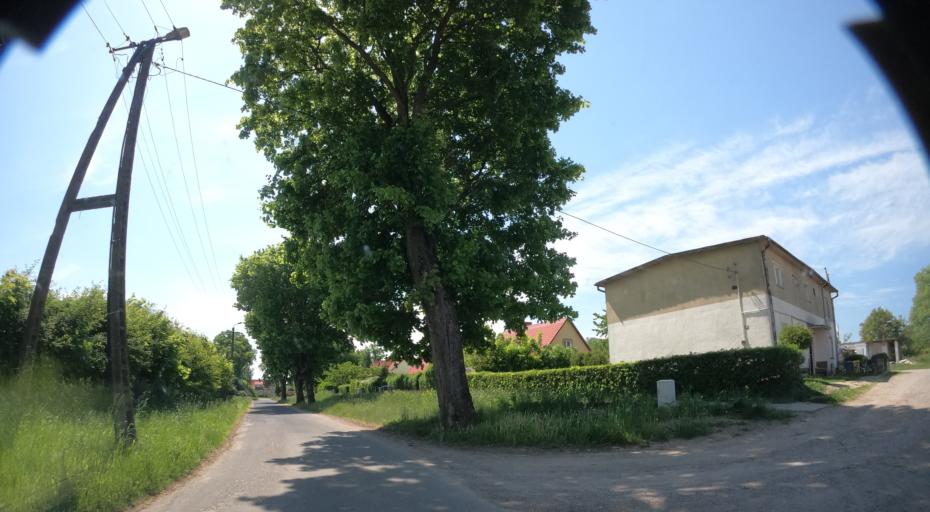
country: PL
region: West Pomeranian Voivodeship
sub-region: Powiat kolobrzeski
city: Dygowo
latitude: 54.1482
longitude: 15.7732
